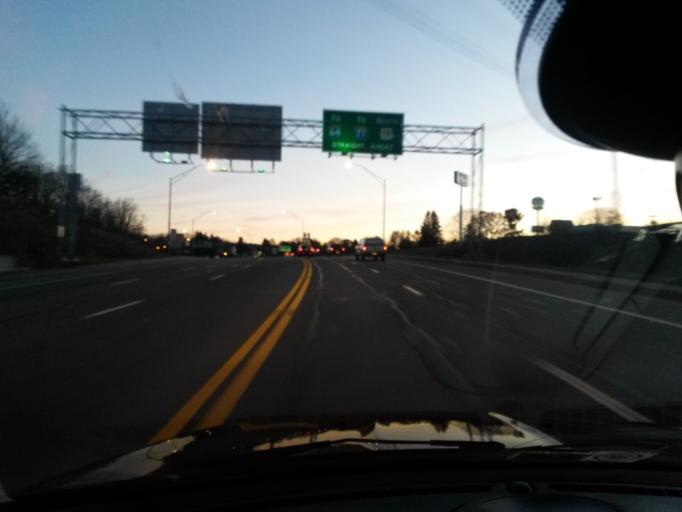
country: US
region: West Virginia
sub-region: Raleigh County
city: Beckley
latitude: 37.7734
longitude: -81.1603
